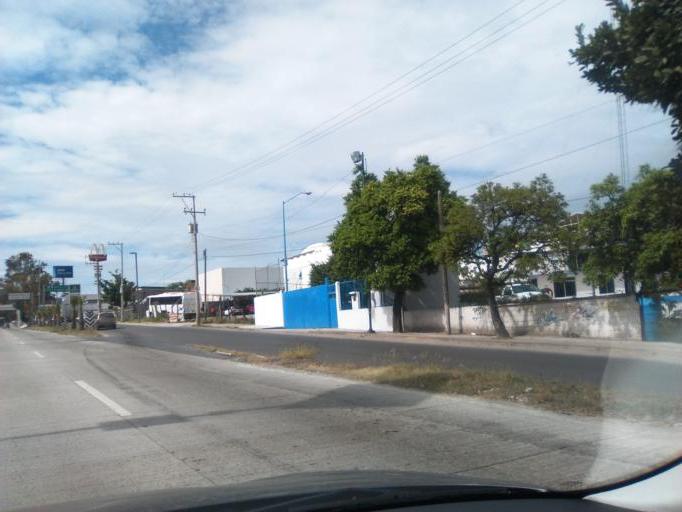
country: MX
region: Guerrero
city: Chilpancingo de los Bravos
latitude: 17.5399
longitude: -99.5014
